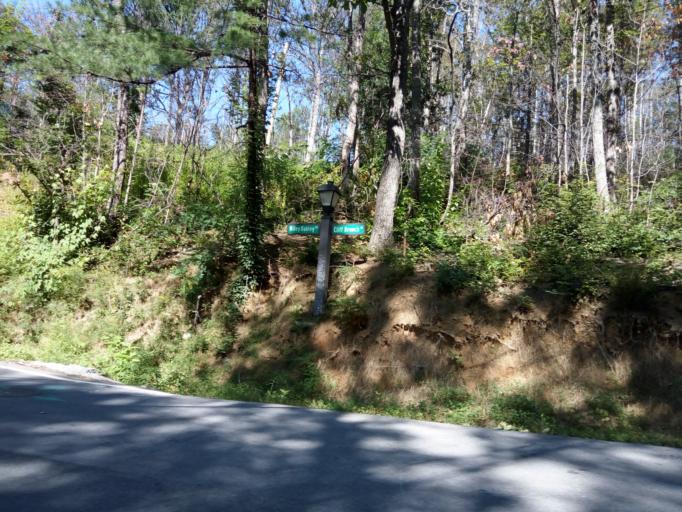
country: US
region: Tennessee
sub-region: Sevier County
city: Gatlinburg
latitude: 35.7130
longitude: -83.5375
